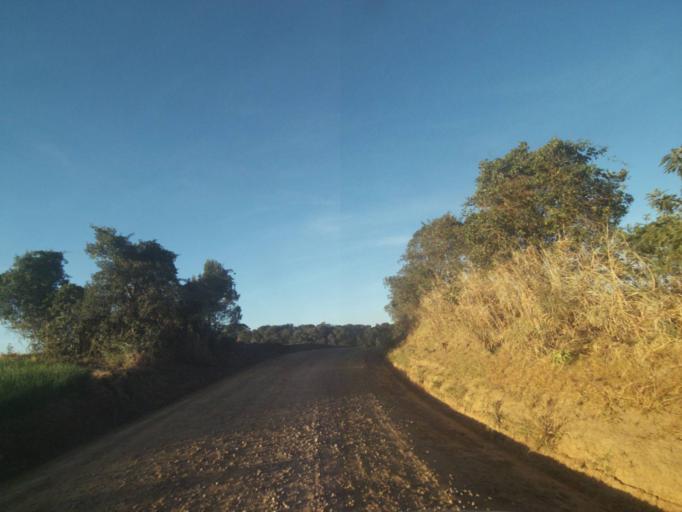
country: BR
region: Parana
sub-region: Tibagi
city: Tibagi
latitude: -24.5448
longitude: -50.5522
